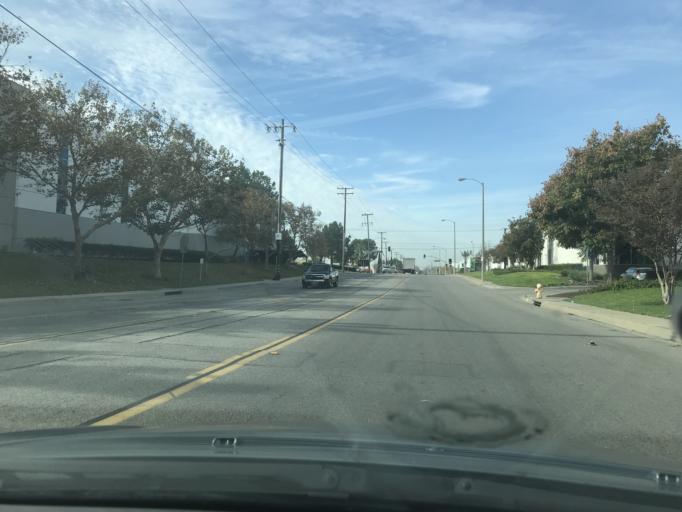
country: US
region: California
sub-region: Los Angeles County
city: Santa Fe Springs
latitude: 33.9318
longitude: -118.0621
